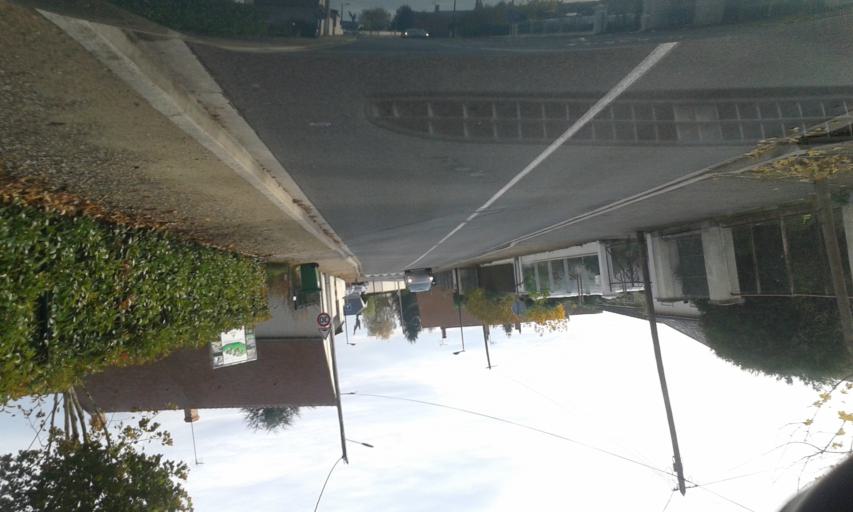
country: FR
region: Centre
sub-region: Departement du Loiret
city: Olivet
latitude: 47.8525
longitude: 1.8931
